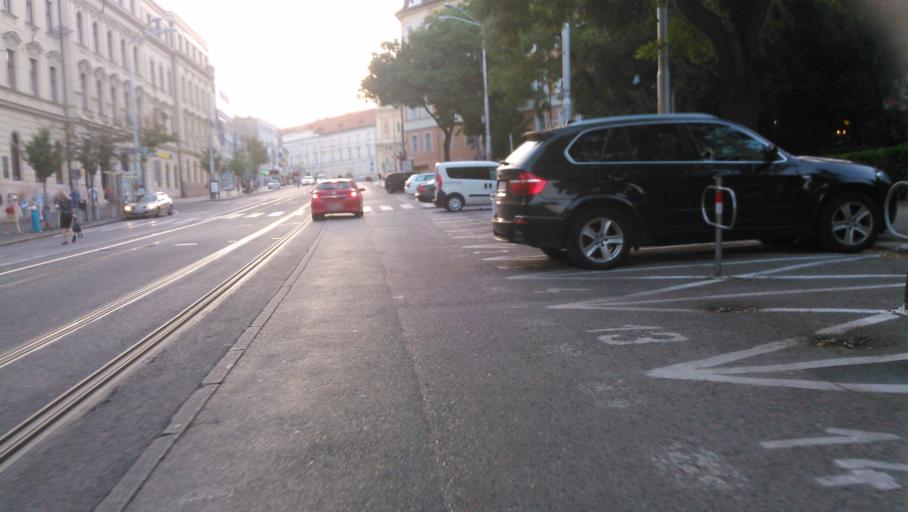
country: SK
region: Bratislavsky
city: Bratislava
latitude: 48.1456
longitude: 17.1096
